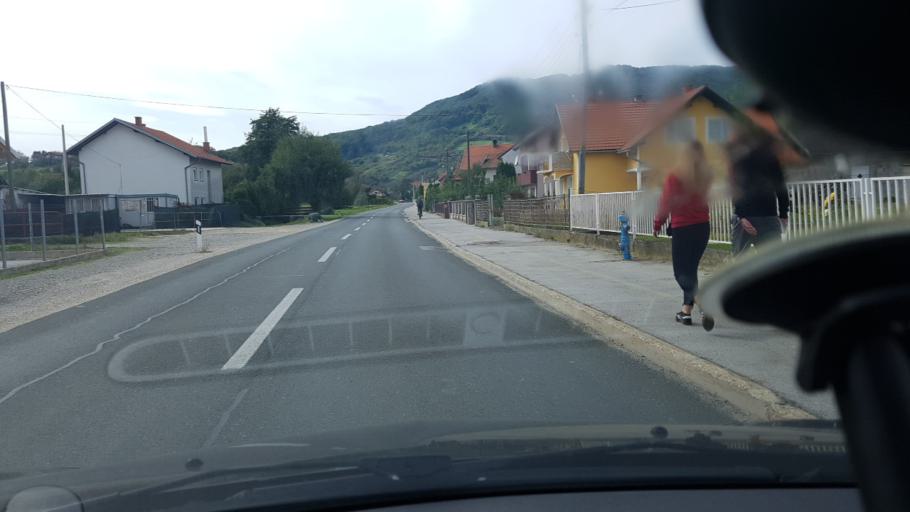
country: HR
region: Varazdinska
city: Remetinec
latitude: 46.1672
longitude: 16.3144
